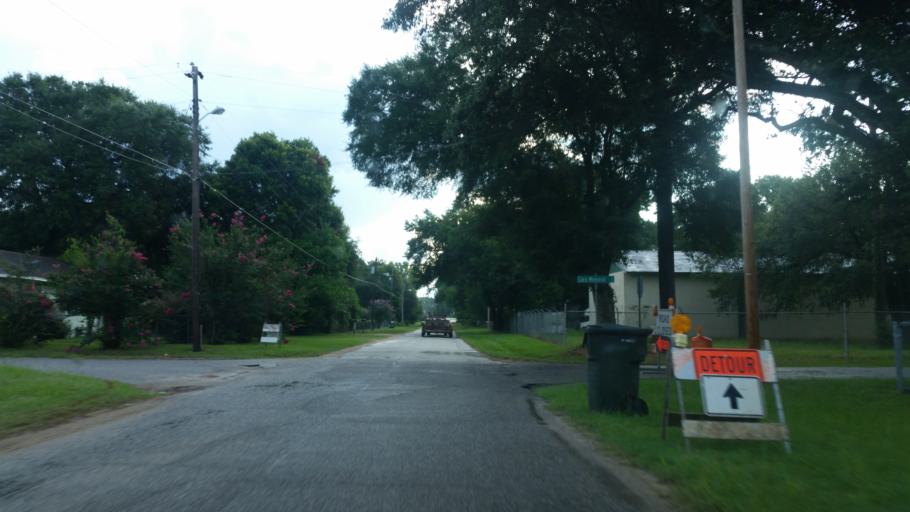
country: US
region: Florida
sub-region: Escambia County
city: Brent
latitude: 30.4584
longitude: -87.2435
